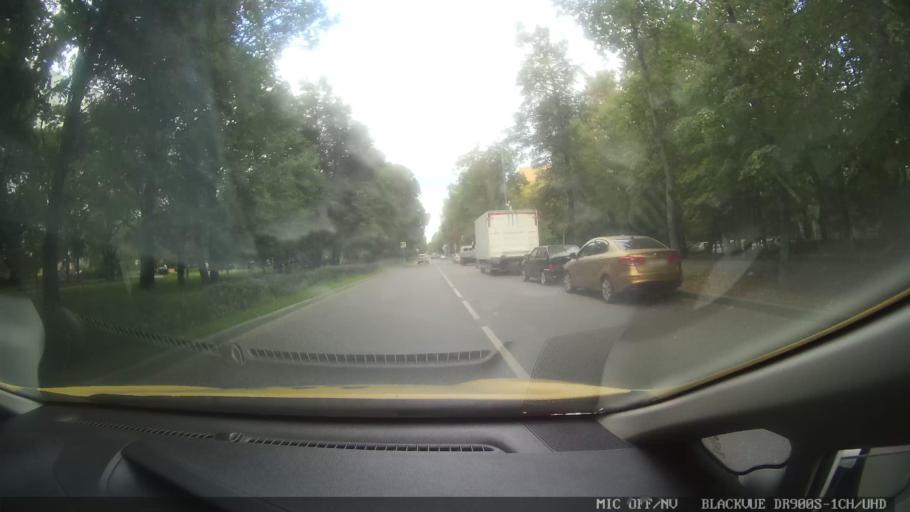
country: RU
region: Moscow
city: Novokuz'minki
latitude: 55.6993
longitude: 37.7780
